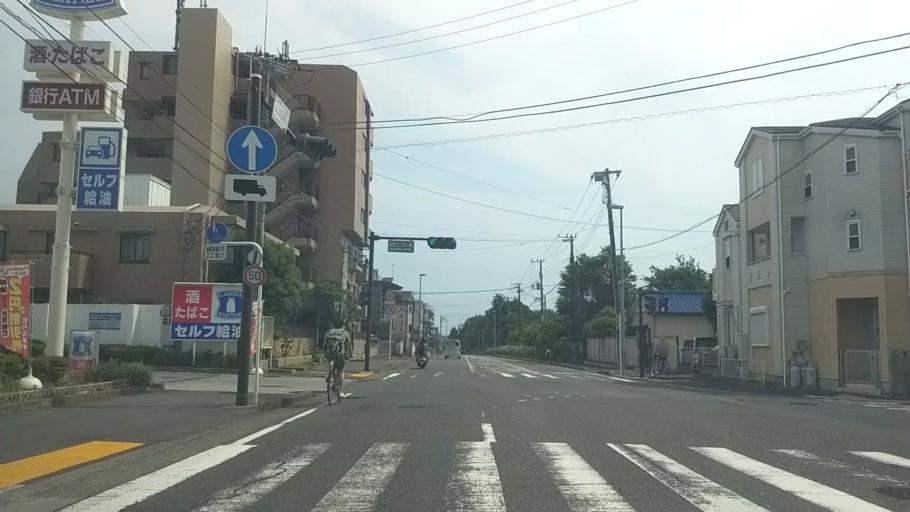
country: JP
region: Kanagawa
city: Fujisawa
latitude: 35.3592
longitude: 139.4785
